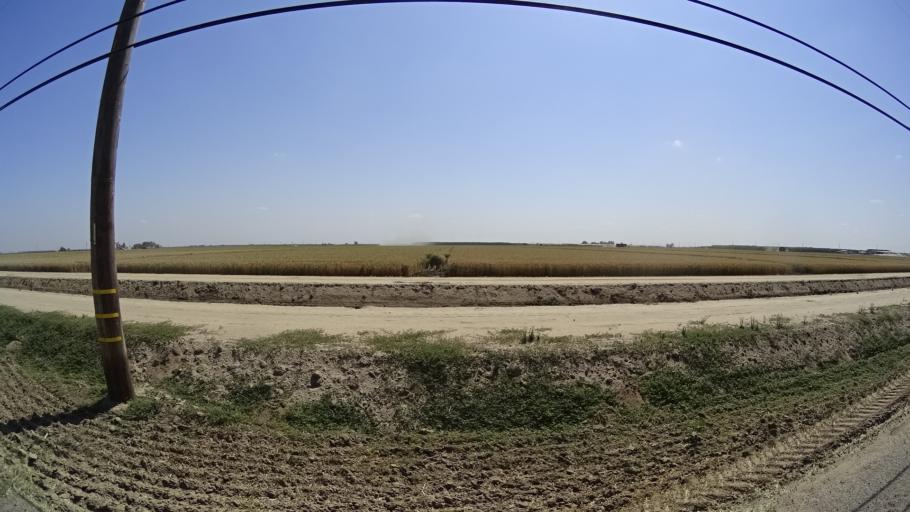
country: US
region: California
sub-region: Kings County
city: Home Garden
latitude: 36.2607
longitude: -119.6190
